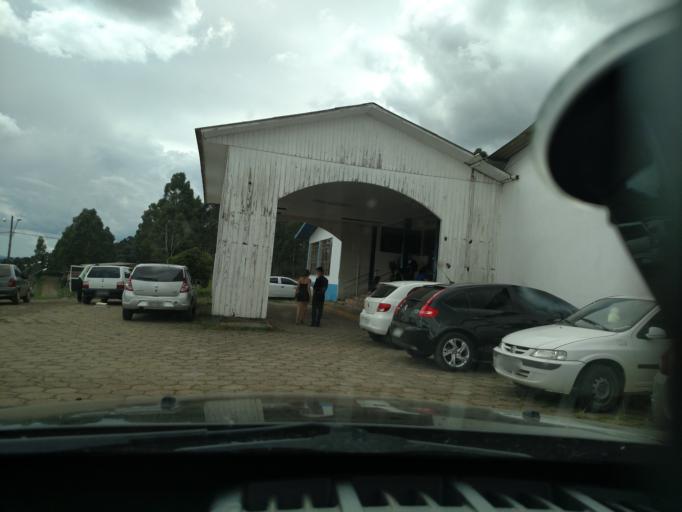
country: BR
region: Santa Catarina
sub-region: Sao Joaquim
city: Sao Joaquim
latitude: -28.2747
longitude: -49.9269
